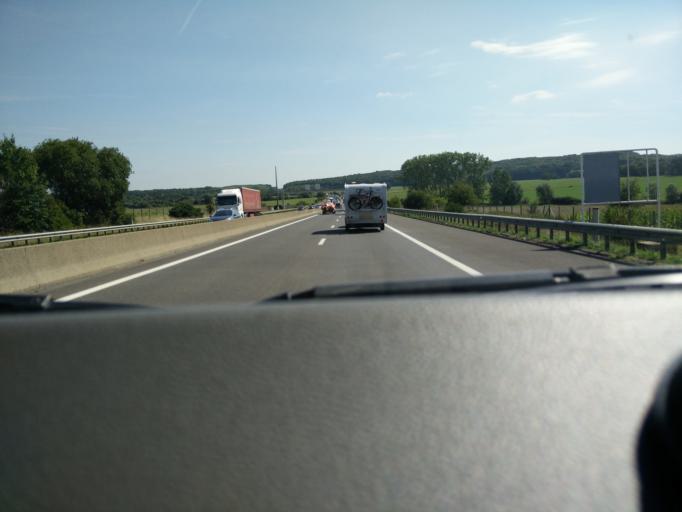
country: LU
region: Luxembourg
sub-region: Canton de Capellen
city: Steinfort
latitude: 49.6370
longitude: 5.9188
